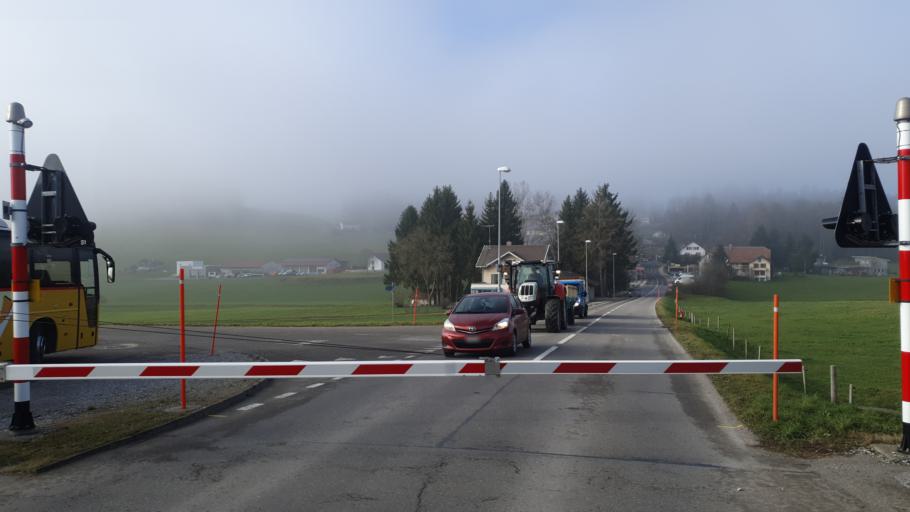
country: CH
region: Fribourg
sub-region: Veveyse District
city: Chatel-Saint-Denis
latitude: 46.5874
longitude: 6.9250
